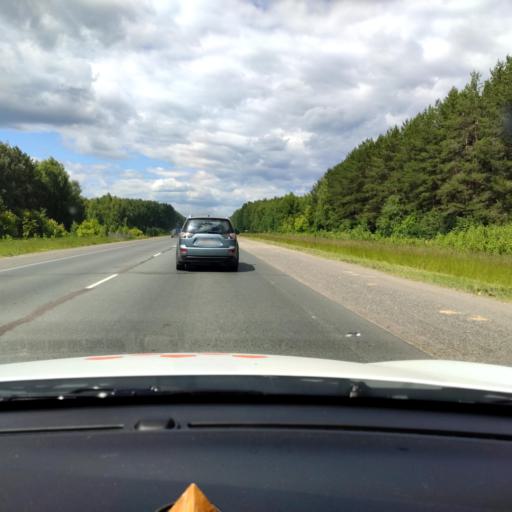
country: RU
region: Mariy-El
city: Pomary
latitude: 55.9343
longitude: 48.3726
